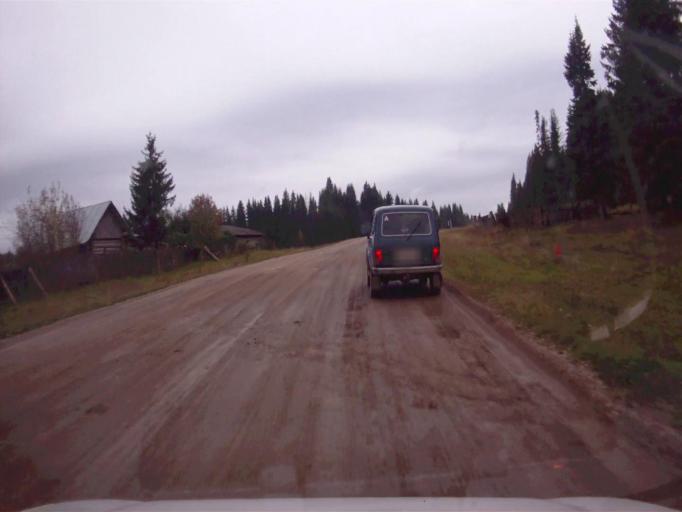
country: RU
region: Chelyabinsk
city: Nyazepetrovsk
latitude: 56.0611
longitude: 59.5636
